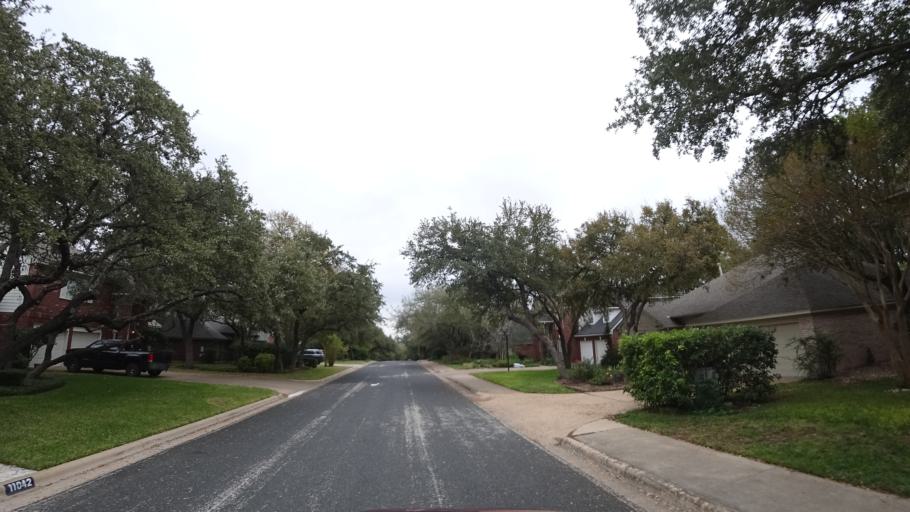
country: US
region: Texas
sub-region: Williamson County
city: Anderson Mill
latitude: 30.4420
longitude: -97.8223
